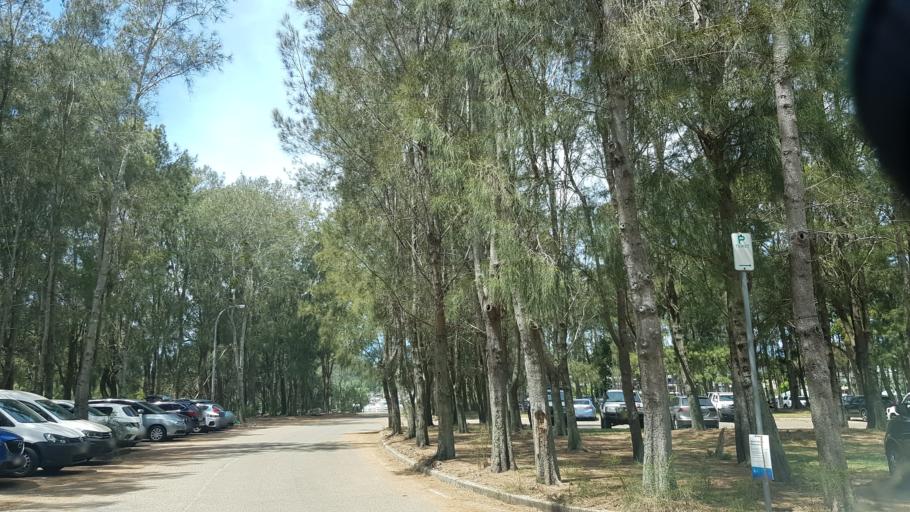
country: AU
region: New South Wales
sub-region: Pittwater
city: Bay View
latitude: -33.6616
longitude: 151.3027
